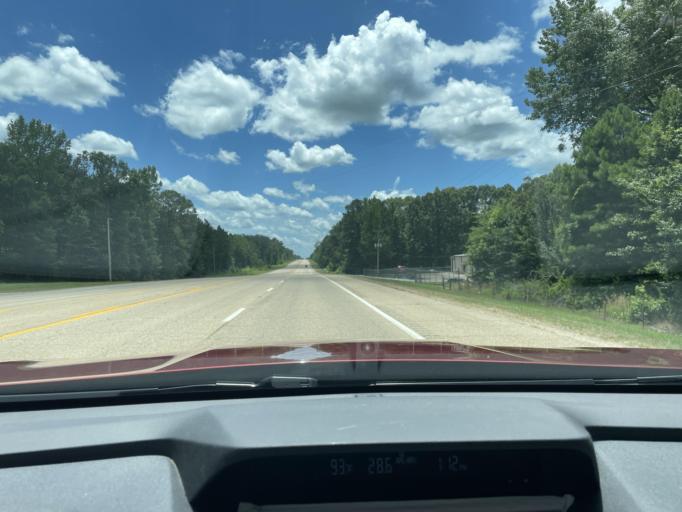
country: US
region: Arkansas
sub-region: Drew County
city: Monticello
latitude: 33.6976
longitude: -91.8069
